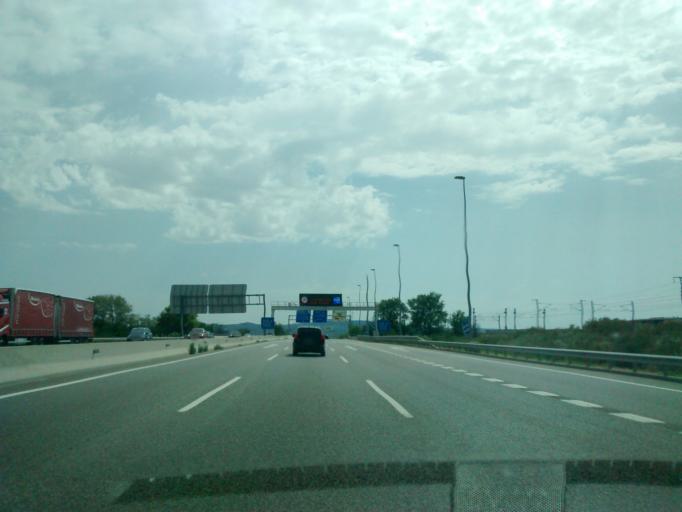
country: ES
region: Aragon
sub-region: Provincia de Zaragoza
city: Montecanal
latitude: 41.6400
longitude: -0.9745
